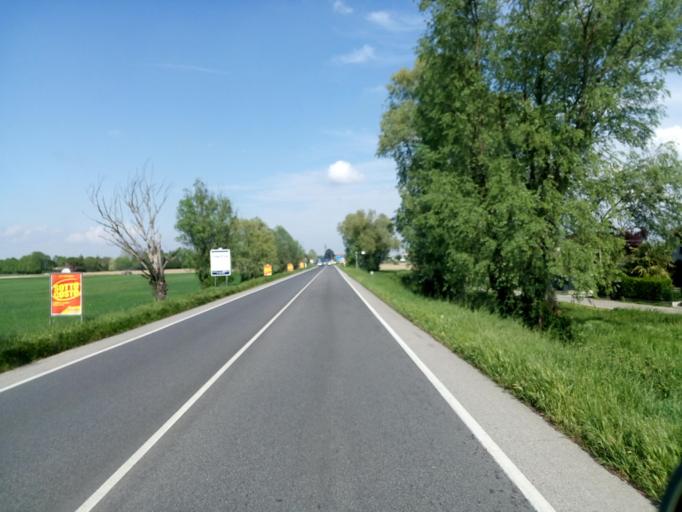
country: IT
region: Veneto
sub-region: Provincia di Verona
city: Angiari
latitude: 45.2122
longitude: 11.3134
